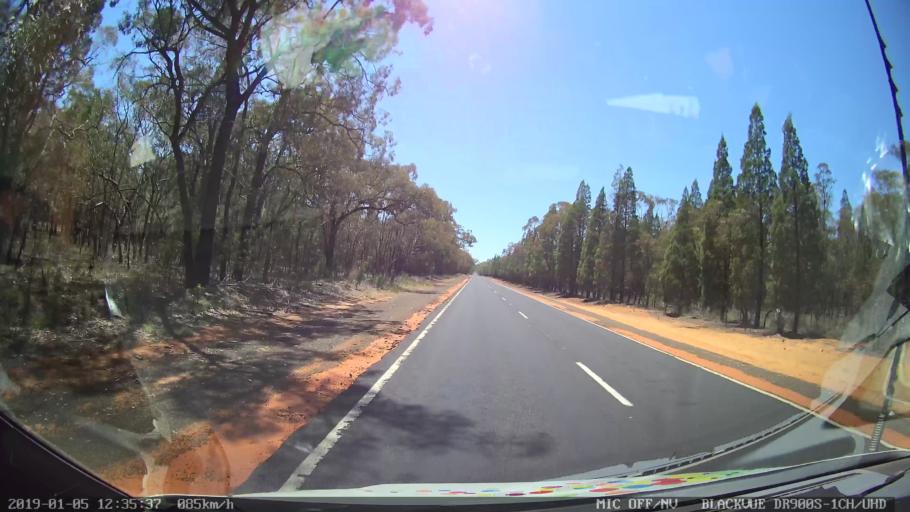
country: AU
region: New South Wales
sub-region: Warrumbungle Shire
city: Coonabarabran
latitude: -31.2091
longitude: 149.4285
